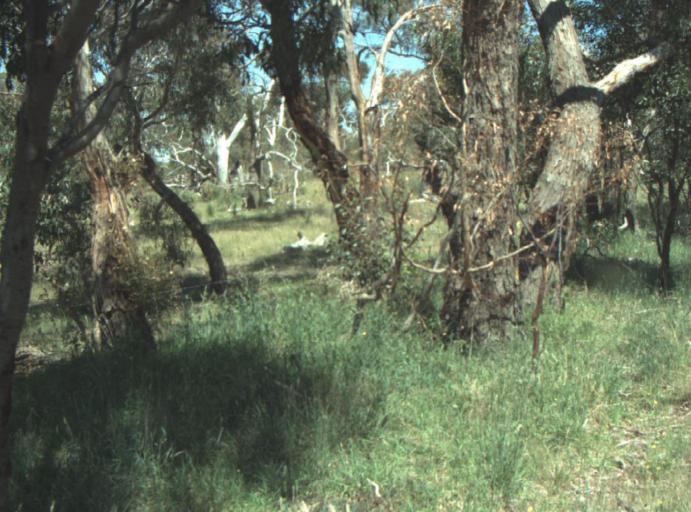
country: AU
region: Victoria
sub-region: Greater Geelong
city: Lara
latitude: -37.8765
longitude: 144.3010
